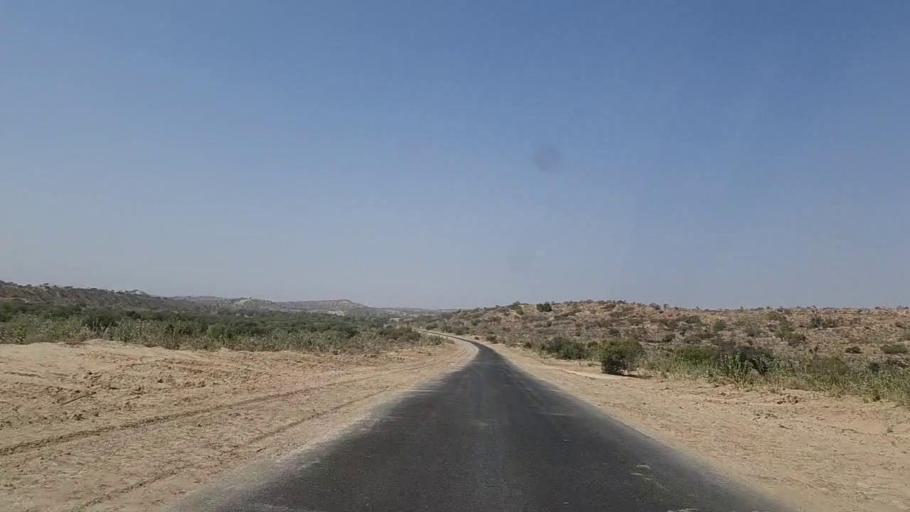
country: PK
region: Sindh
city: Diplo
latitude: 24.5803
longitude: 69.5074
